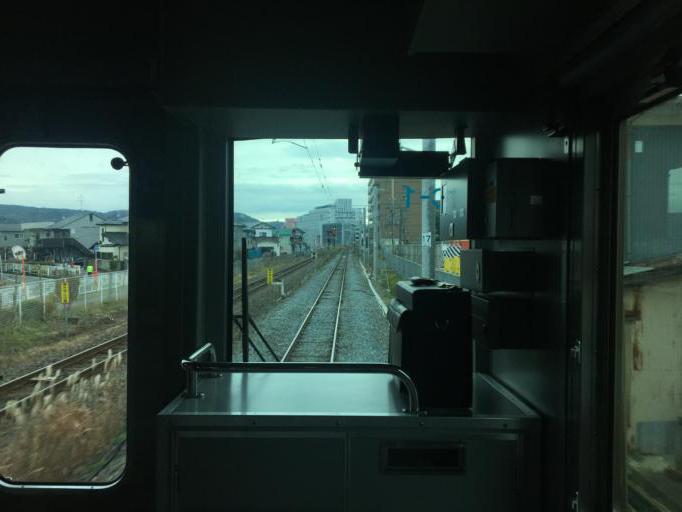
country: JP
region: Miyagi
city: Ishinomaki
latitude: 38.4380
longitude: 141.2965
